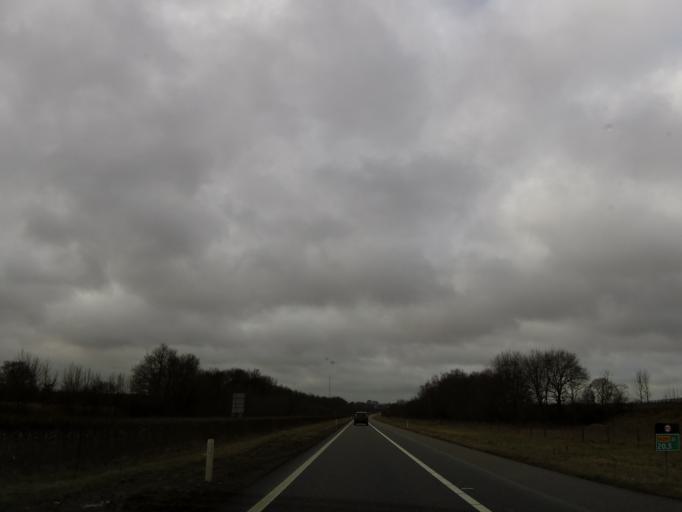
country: NL
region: Limburg
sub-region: Gemeente Simpelveld
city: Simpelveld
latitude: 50.8310
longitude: 6.0017
